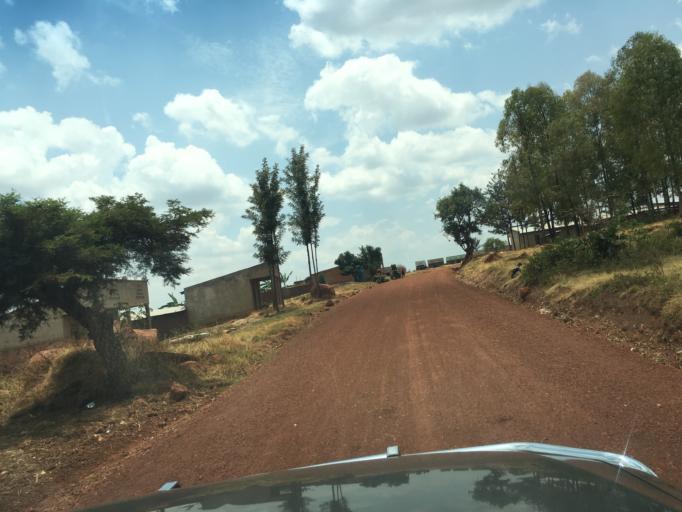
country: RW
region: Eastern Province
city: Kibungo
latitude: -2.2445
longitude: 30.7479
